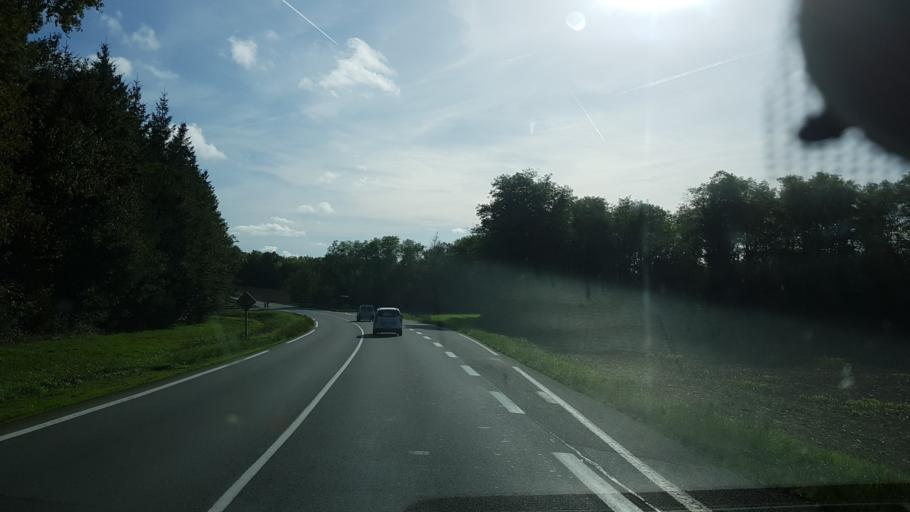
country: FR
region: Poitou-Charentes
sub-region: Departement de la Charente
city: Saint-Claud
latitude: 45.8681
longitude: 0.4658
